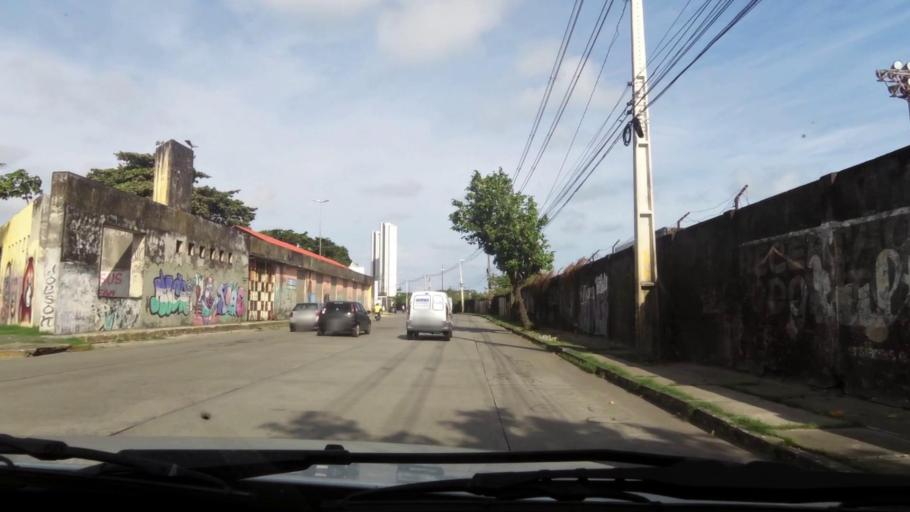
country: BR
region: Pernambuco
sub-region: Recife
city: Recife
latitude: -8.0725
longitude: -34.8815
